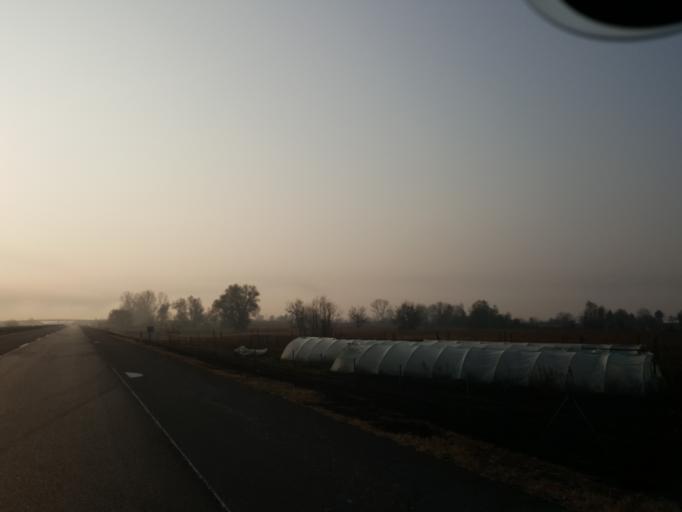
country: RS
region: Central Serbia
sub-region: Jablanicki Okrug
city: Leskovac
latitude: 43.0407
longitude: 21.9929
